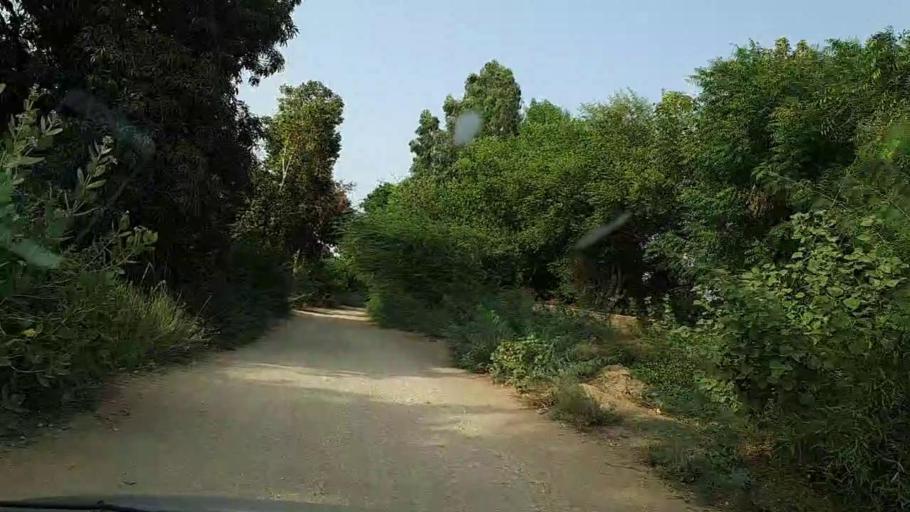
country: PK
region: Sindh
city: Kotri
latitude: 25.2386
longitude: 68.2647
